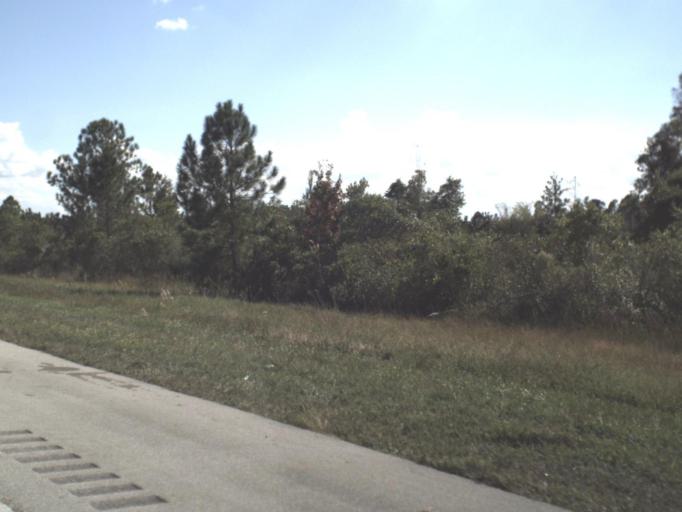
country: US
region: Florida
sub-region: Osceola County
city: Saint Cloud
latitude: 27.9503
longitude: -81.0879
